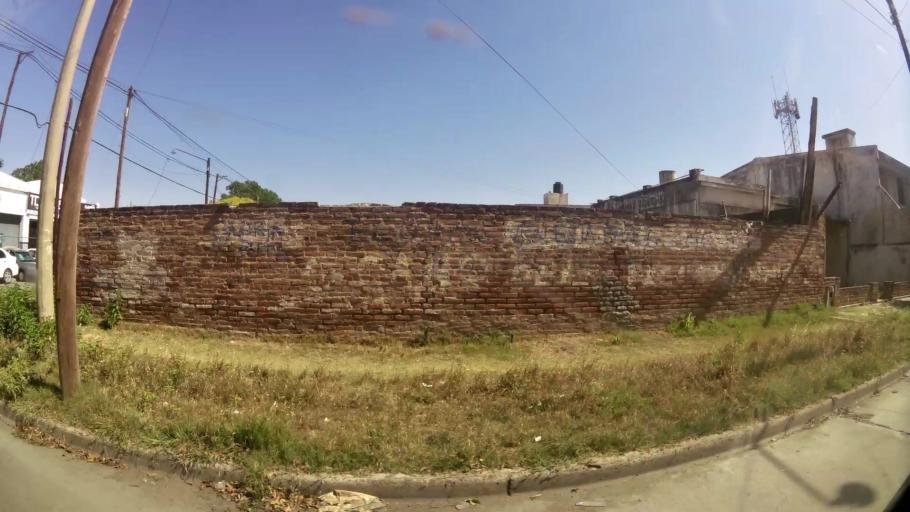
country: AR
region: Cordoba
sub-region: Departamento de Capital
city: Cordoba
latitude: -31.3691
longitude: -64.1750
